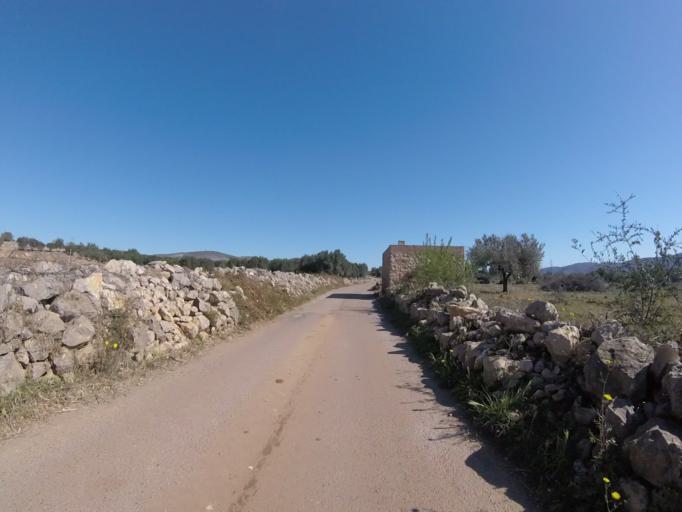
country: ES
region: Valencia
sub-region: Provincia de Castello
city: Santa Magdalena de Pulpis
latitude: 40.3542
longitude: 0.2825
